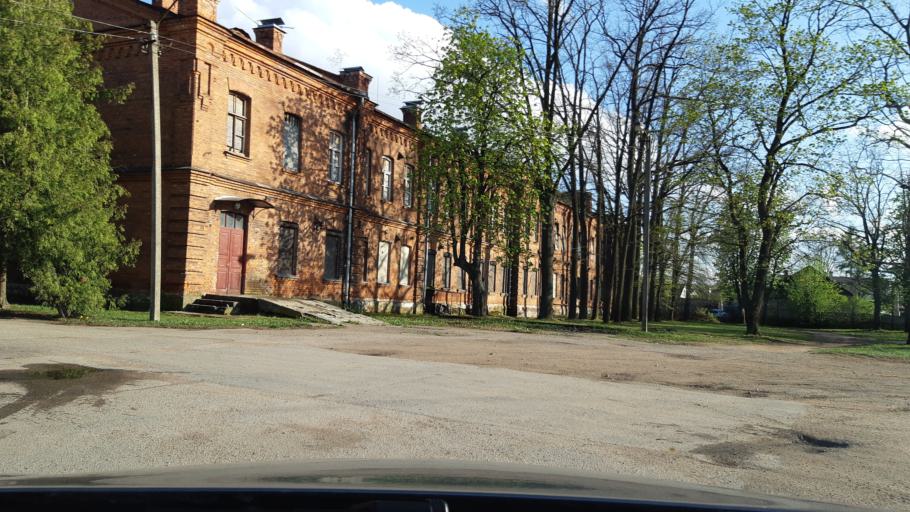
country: LT
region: Kauno apskritis
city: Dainava (Kaunas)
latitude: 54.8673
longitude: 23.9660
